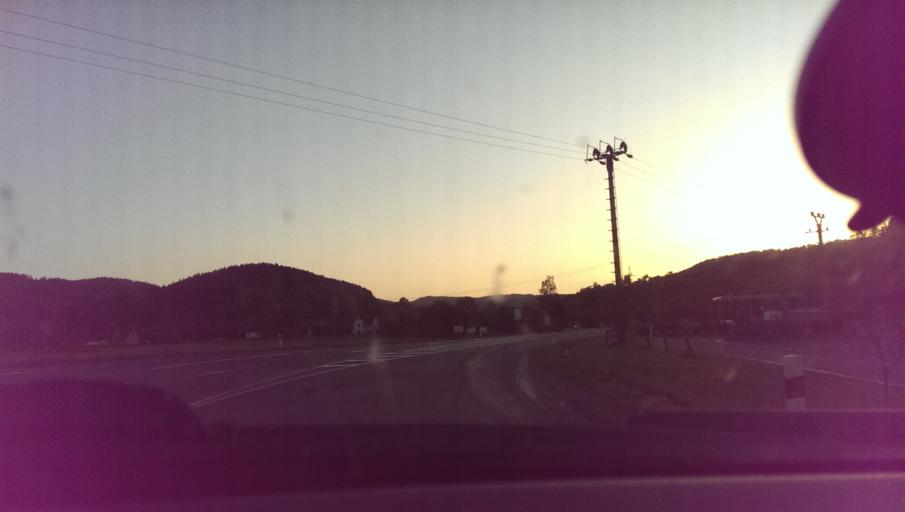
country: CZ
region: Zlin
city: Jablunka
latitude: 49.4172
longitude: 17.9558
